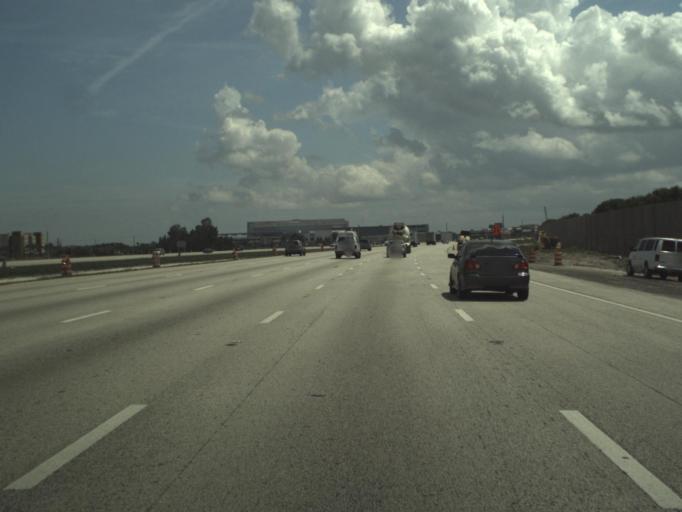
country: US
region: Florida
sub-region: Broward County
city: Sunshine Ranches
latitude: 26.0010
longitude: -80.3396
